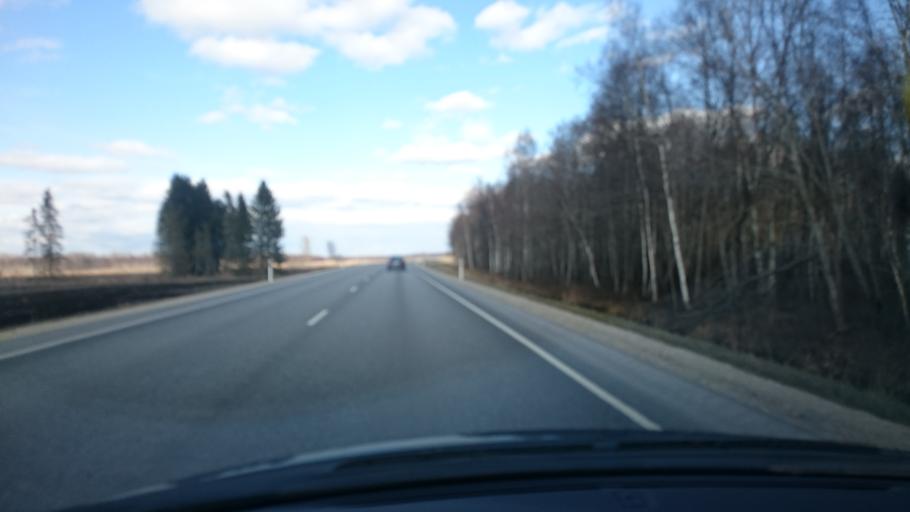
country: EE
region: Laeaene
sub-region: Lihula vald
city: Lihula
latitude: 58.7816
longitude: 24.0002
